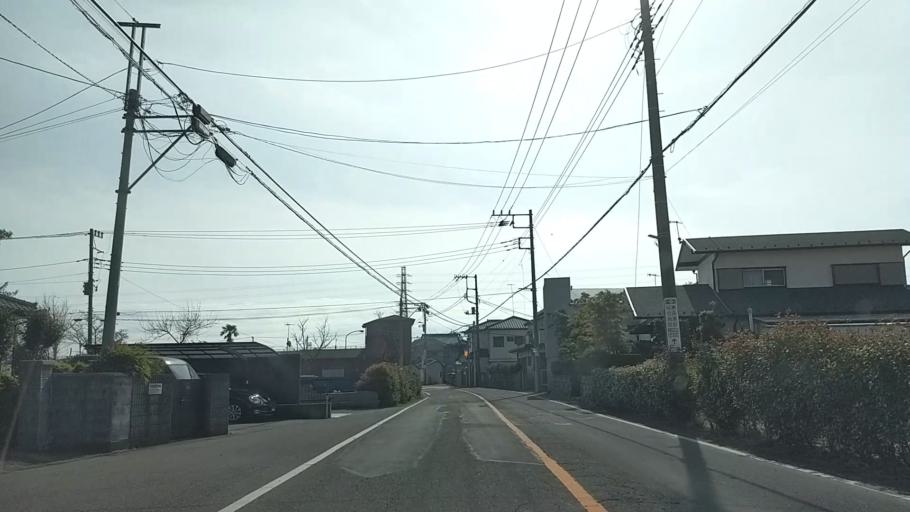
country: JP
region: Kanagawa
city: Chigasaki
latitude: 35.3542
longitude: 139.3847
